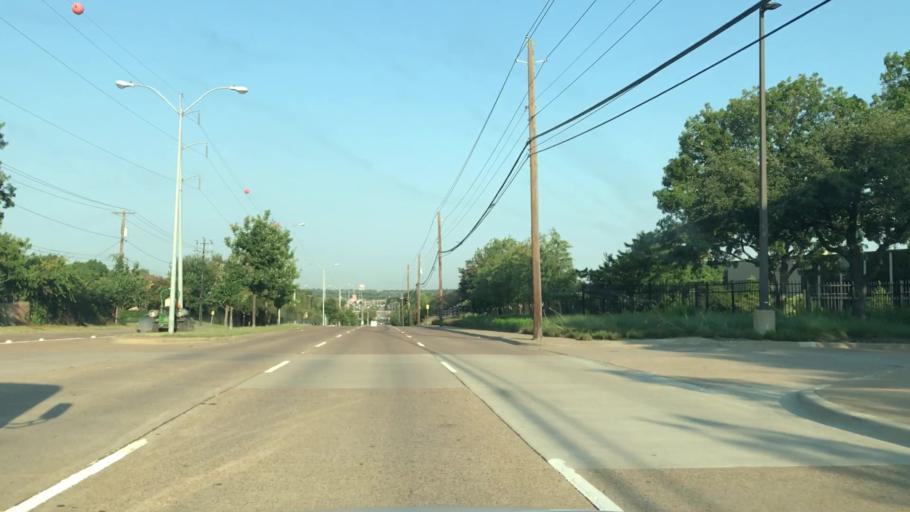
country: US
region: Texas
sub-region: Dallas County
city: Richardson
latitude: 32.9093
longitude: -96.7533
